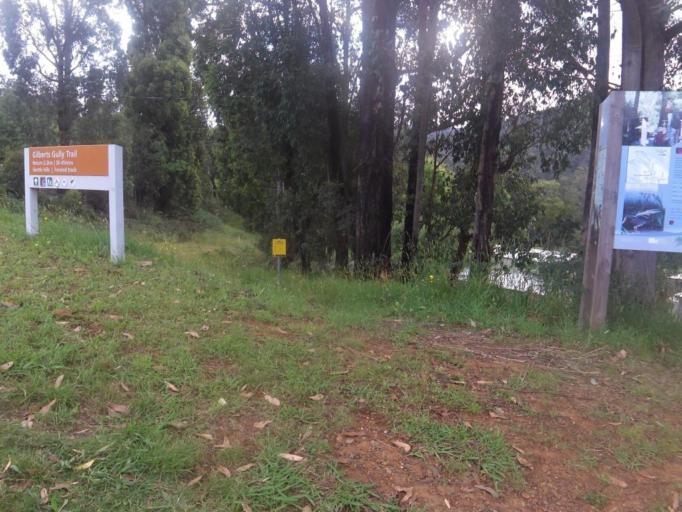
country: AU
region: Victoria
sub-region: Yarra Ranges
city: Millgrove
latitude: -37.5103
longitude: 145.7393
